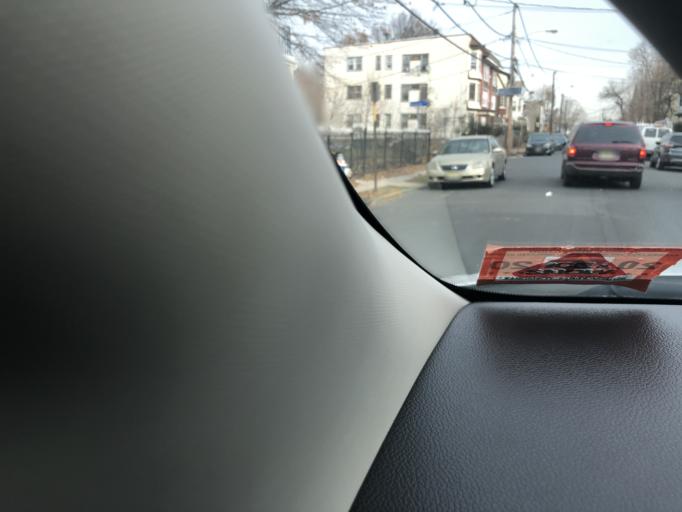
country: US
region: New Jersey
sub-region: Essex County
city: Irvington
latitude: 40.7266
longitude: -74.2166
